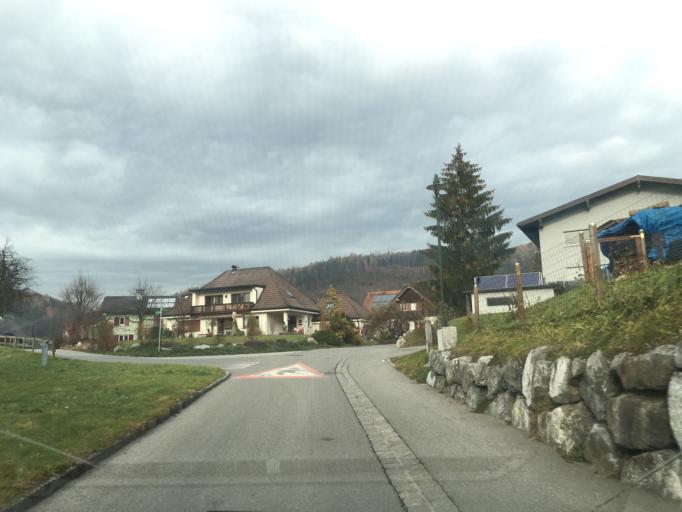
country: AT
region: Vorarlberg
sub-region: Politischer Bezirk Feldkirch
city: Weiler
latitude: 47.3061
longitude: 9.6538
